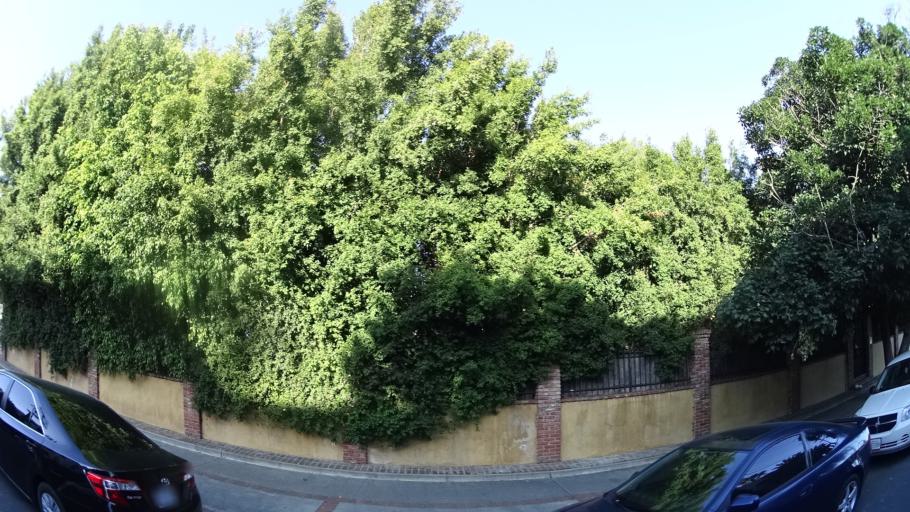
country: US
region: California
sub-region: Los Angeles County
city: Van Nuys
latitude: 34.1690
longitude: -118.4443
